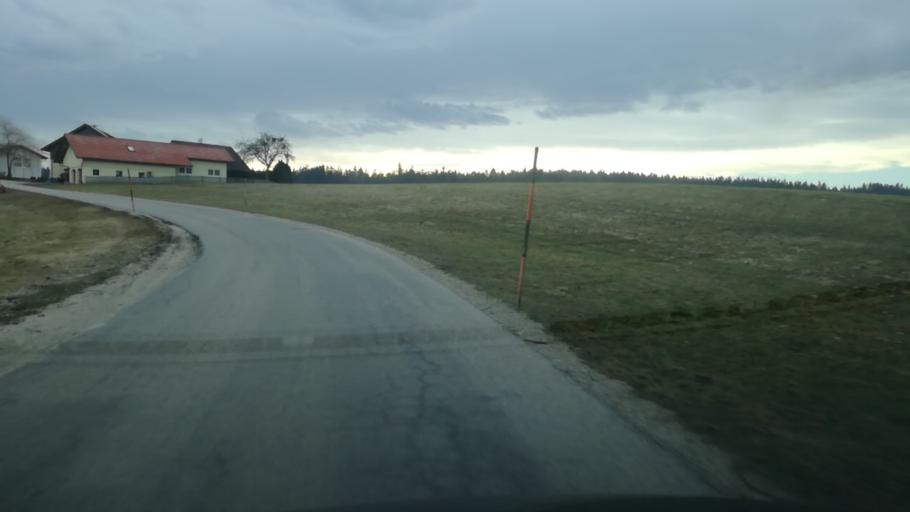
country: AT
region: Upper Austria
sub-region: Politischer Bezirk Vocklabruck
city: Frankenburg
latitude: 48.0606
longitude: 13.5124
